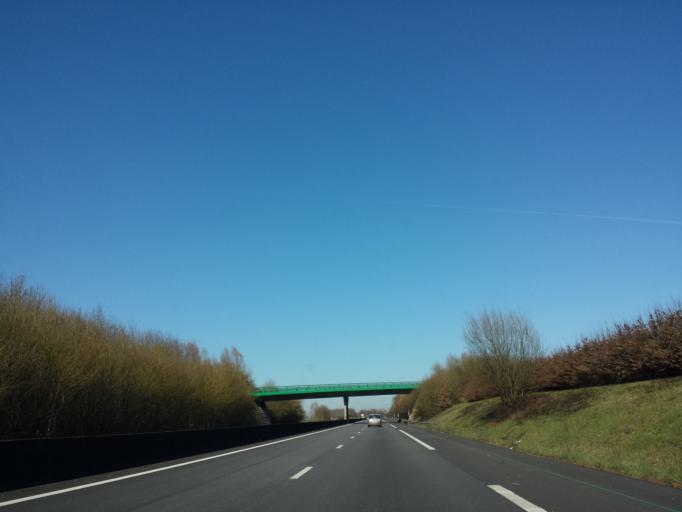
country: FR
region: Picardie
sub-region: Departement de l'Oise
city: Saint-Crepin-Ibouvillers
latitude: 49.2762
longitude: 2.0854
